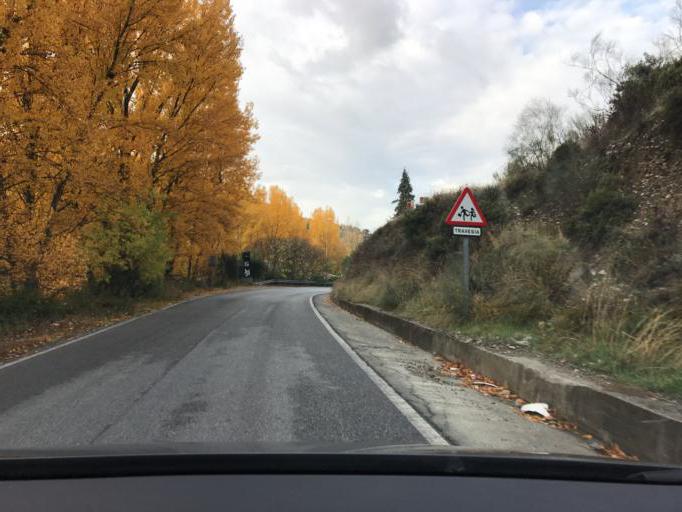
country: ES
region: Andalusia
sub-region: Provincia de Granada
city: Dudar
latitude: 37.1877
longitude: -3.4796
